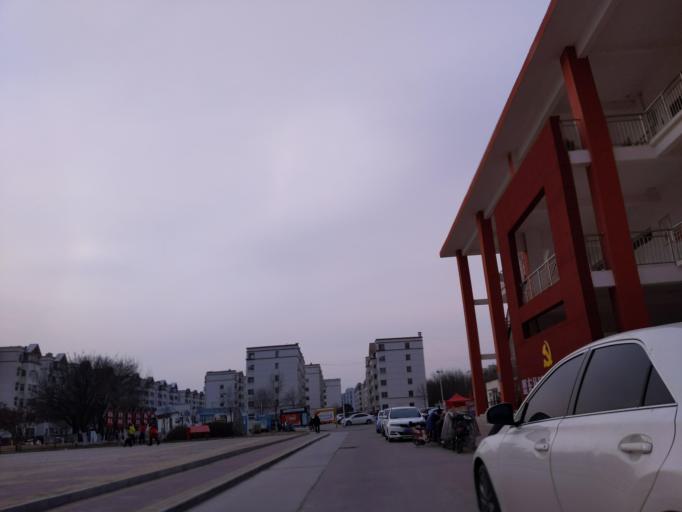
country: CN
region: Henan Sheng
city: Zhongyuanlu
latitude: 35.7565
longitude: 115.0543
